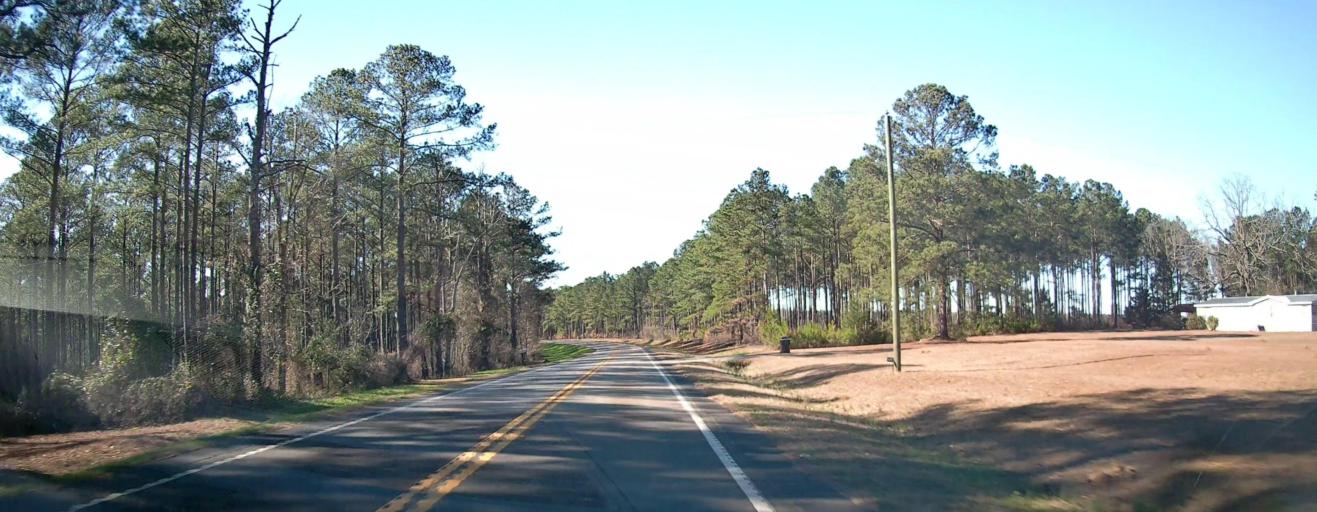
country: US
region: Georgia
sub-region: Schley County
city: Ellaville
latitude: 32.1901
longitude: -84.2103
